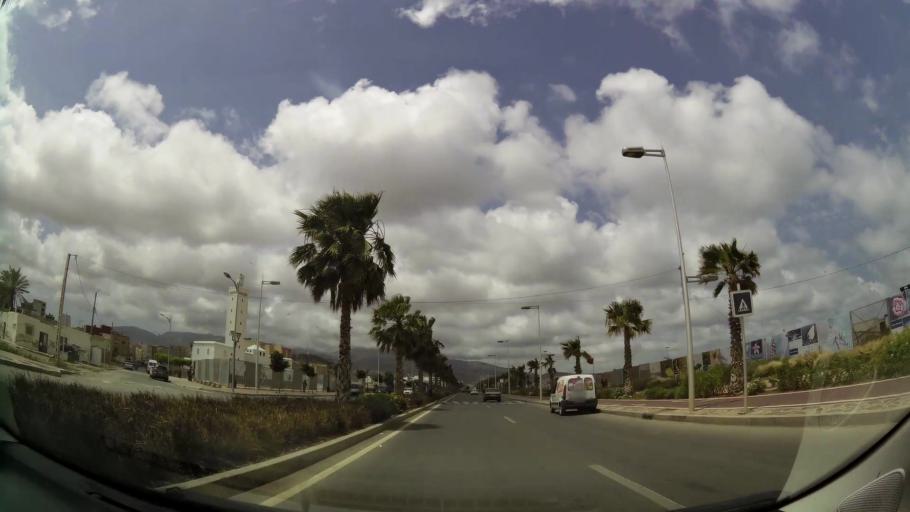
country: MA
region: Oriental
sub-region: Nador
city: Nador
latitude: 35.1718
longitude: -2.9161
